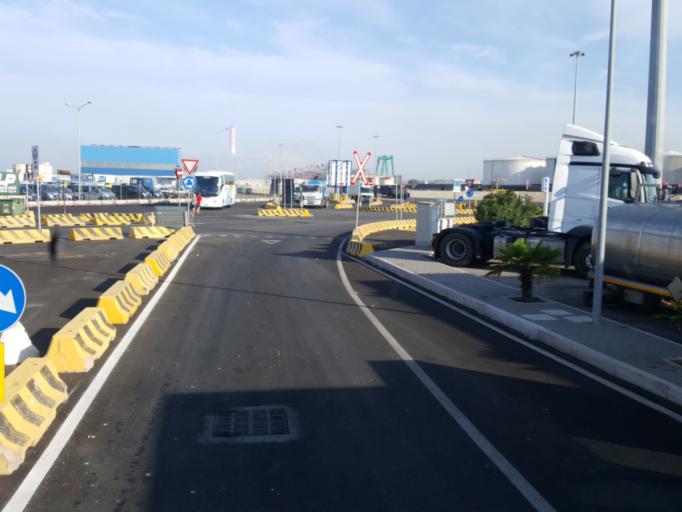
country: IT
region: Latium
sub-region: Citta metropolitana di Roma Capitale
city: Civitavecchia
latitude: 42.1051
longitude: 11.7788
